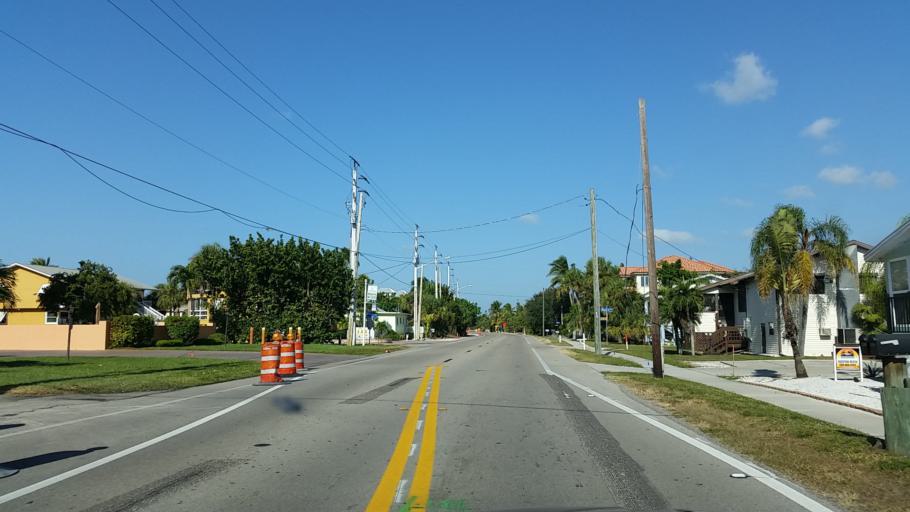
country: US
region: Florida
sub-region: Lee County
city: Fort Myers Beach
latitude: 26.4379
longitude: -81.9228
